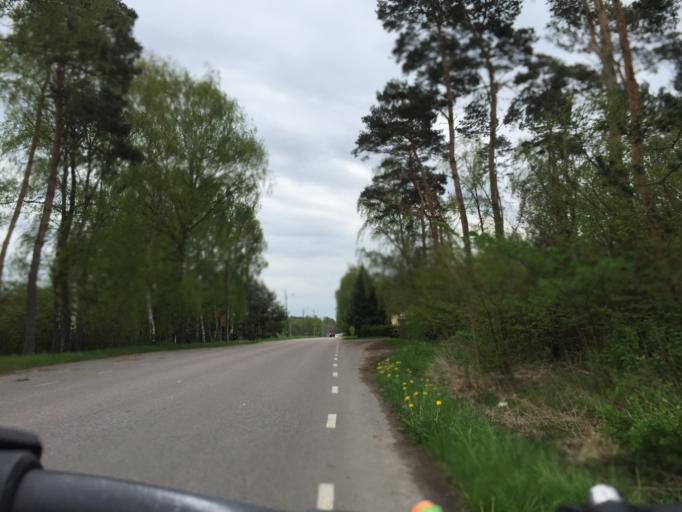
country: SE
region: Skane
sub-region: Lunds Kommun
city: Veberod
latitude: 55.6452
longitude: 13.4674
